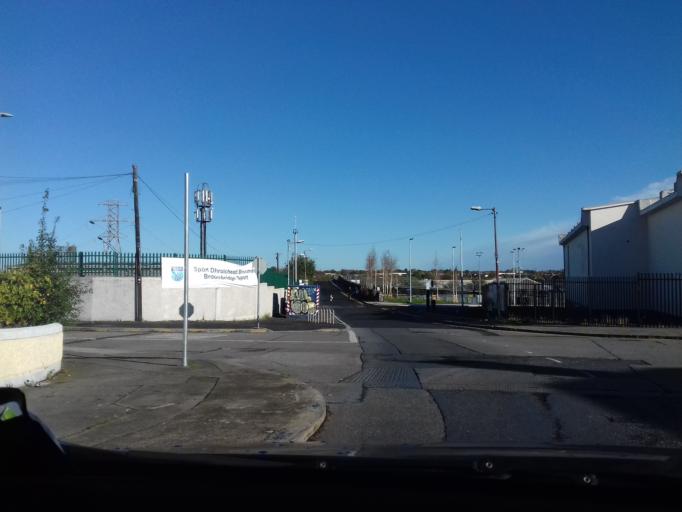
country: IE
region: Leinster
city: Cabra
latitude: 53.3718
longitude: -6.2999
